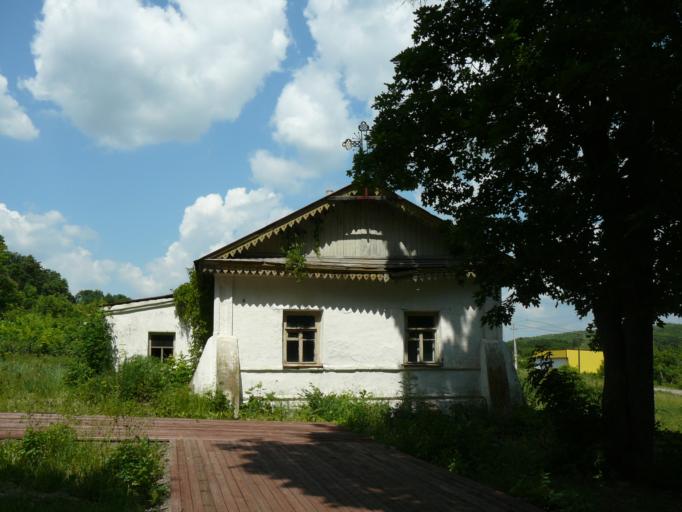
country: RU
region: Penza
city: Tamala
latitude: 52.3926
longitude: 43.3821
